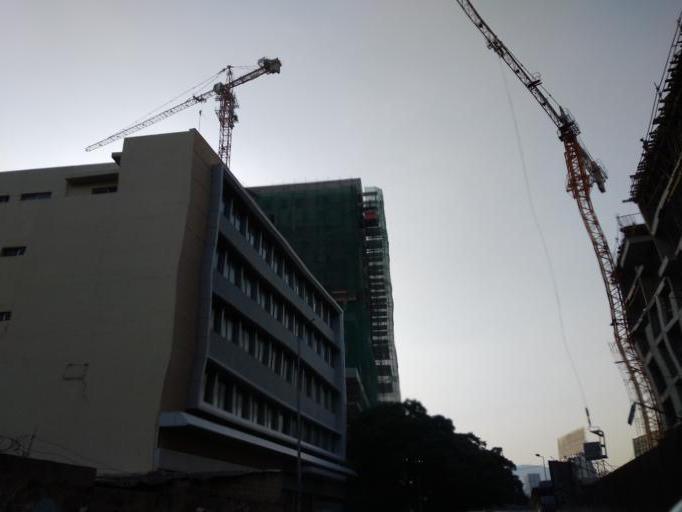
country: LB
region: Beyrouth
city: Beirut
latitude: 33.8812
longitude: 35.5296
